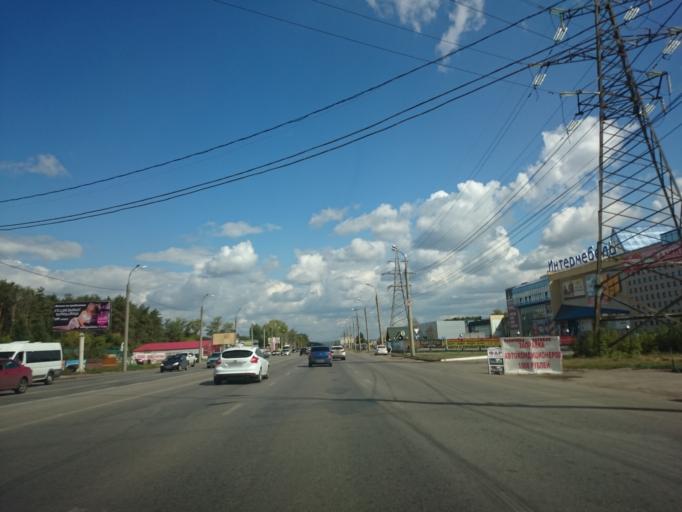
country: RU
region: Samara
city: Samara
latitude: 53.2620
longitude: 50.2410
